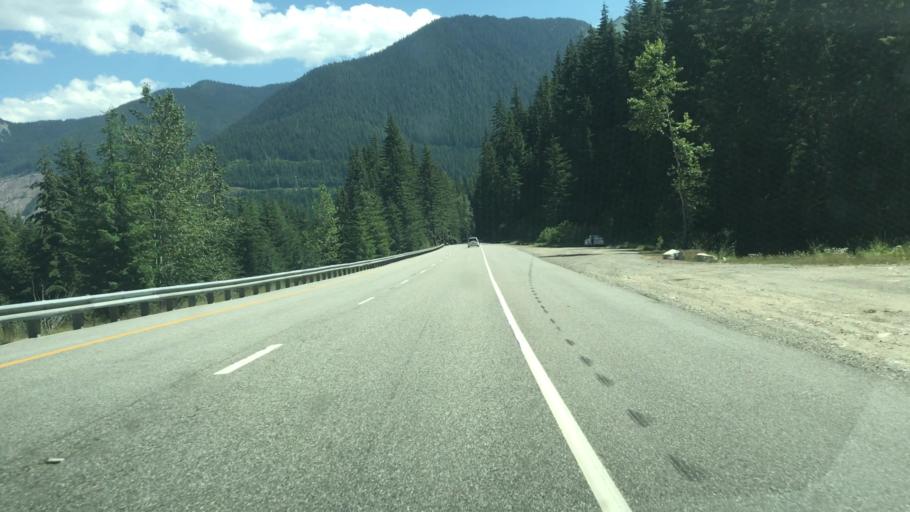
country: US
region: Washington
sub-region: Chelan County
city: Leavenworth
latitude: 47.7820
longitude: -121.0271
